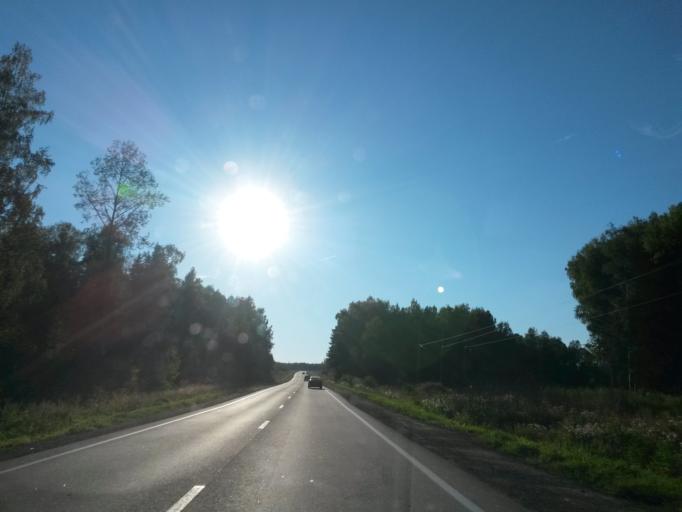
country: RU
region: Jaroslavl
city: Gavrilov-Yam
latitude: 57.2685
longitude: 39.9766
